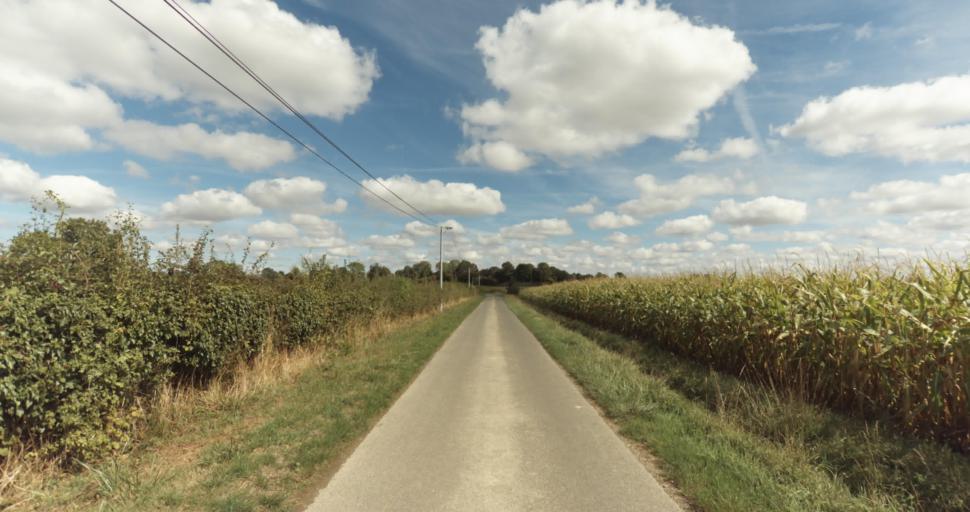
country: FR
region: Lower Normandy
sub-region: Departement du Calvados
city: Orbec
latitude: 48.9213
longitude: 0.3713
